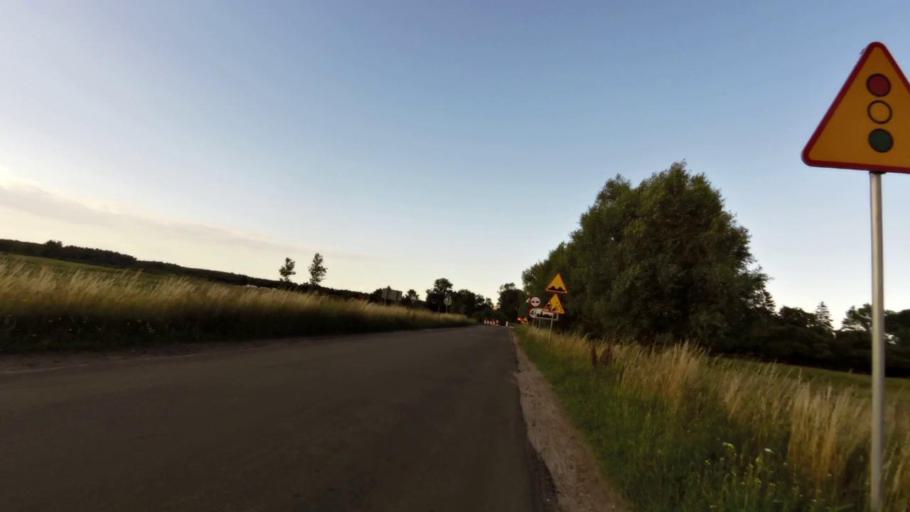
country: PL
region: West Pomeranian Voivodeship
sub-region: Powiat slawienski
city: Darlowo
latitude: 54.4025
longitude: 16.3672
